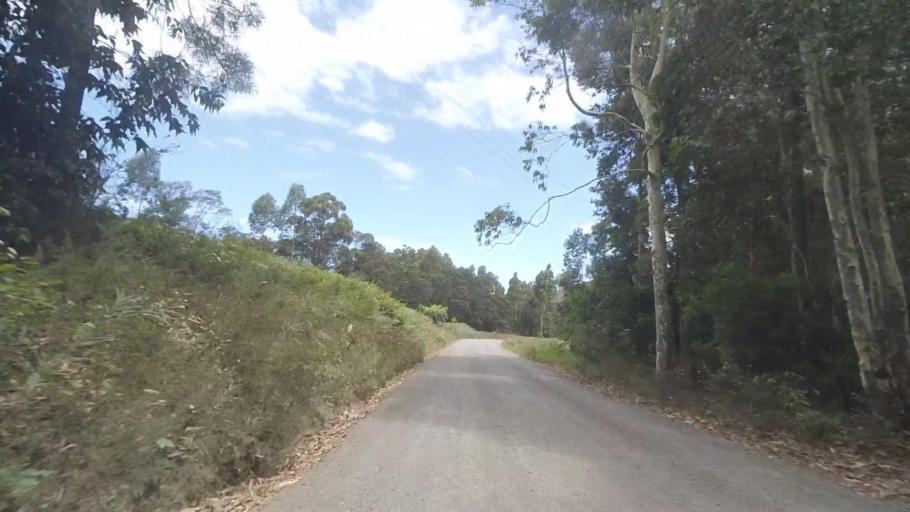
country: AU
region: New South Wales
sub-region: Shoalhaven Shire
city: Milton
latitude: -35.4363
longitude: 150.3308
